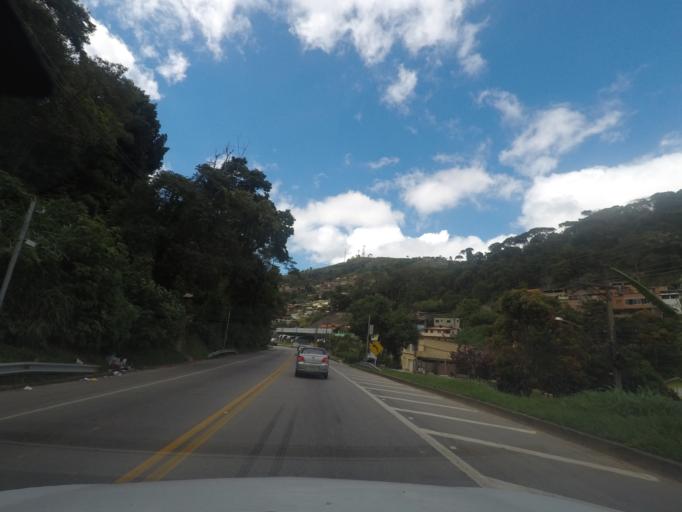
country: BR
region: Rio de Janeiro
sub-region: Teresopolis
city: Teresopolis
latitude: -22.3972
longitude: -42.9547
